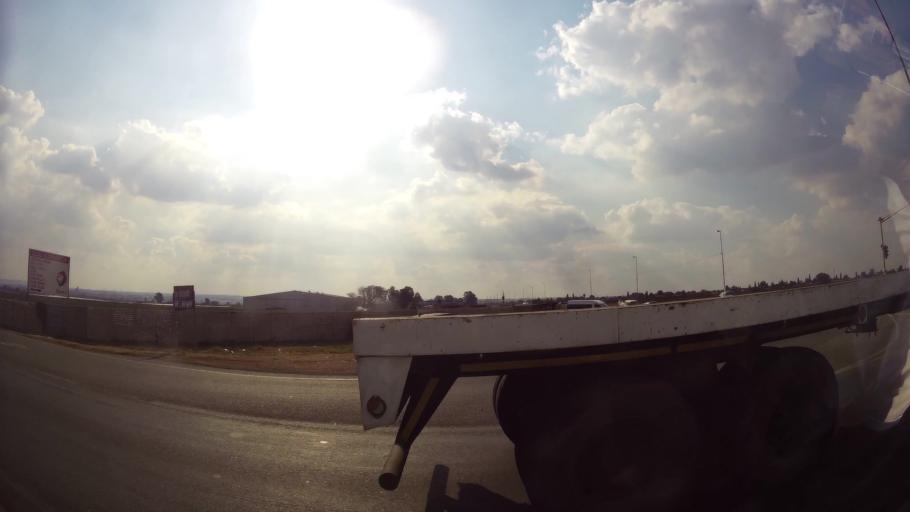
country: ZA
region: Gauteng
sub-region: Ekurhuleni Metropolitan Municipality
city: Germiston
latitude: -26.2899
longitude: 28.2291
